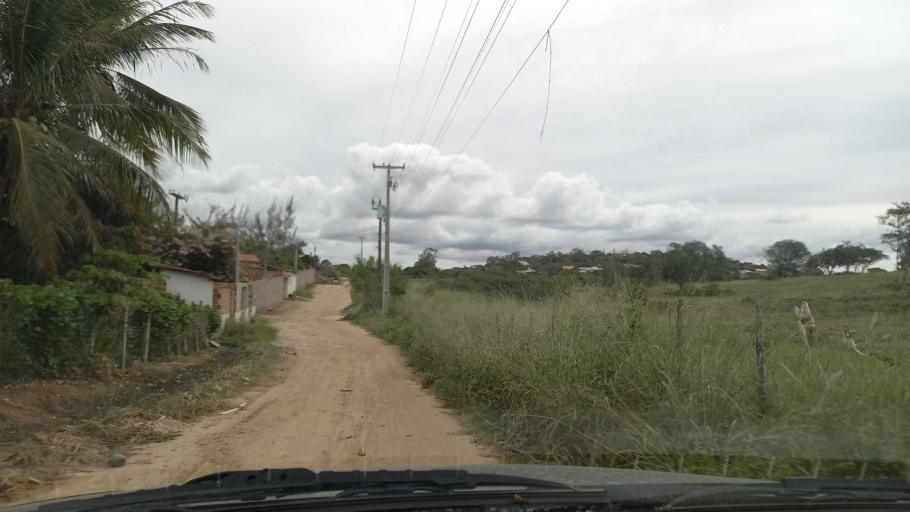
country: BR
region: Pernambuco
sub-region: Gravata
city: Gravata
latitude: -8.1915
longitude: -35.5956
